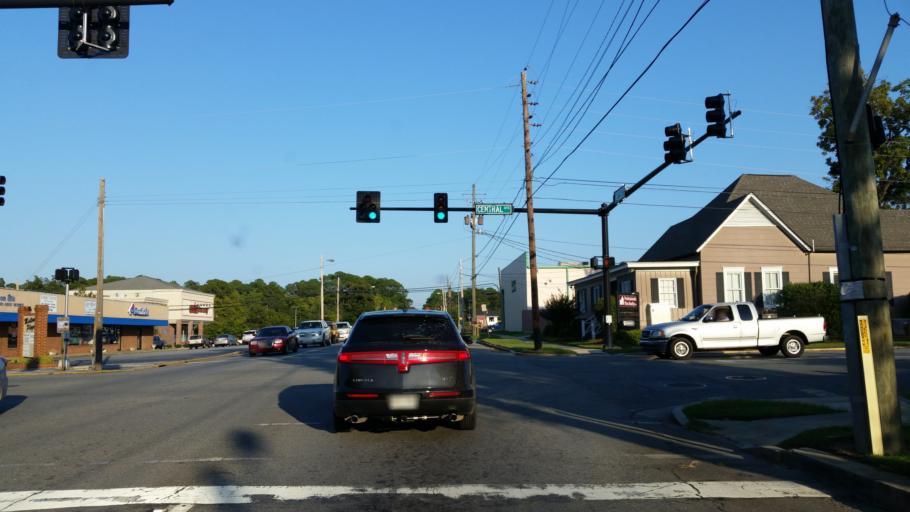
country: US
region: Georgia
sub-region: Tift County
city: Tifton
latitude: 31.4601
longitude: -83.5088
